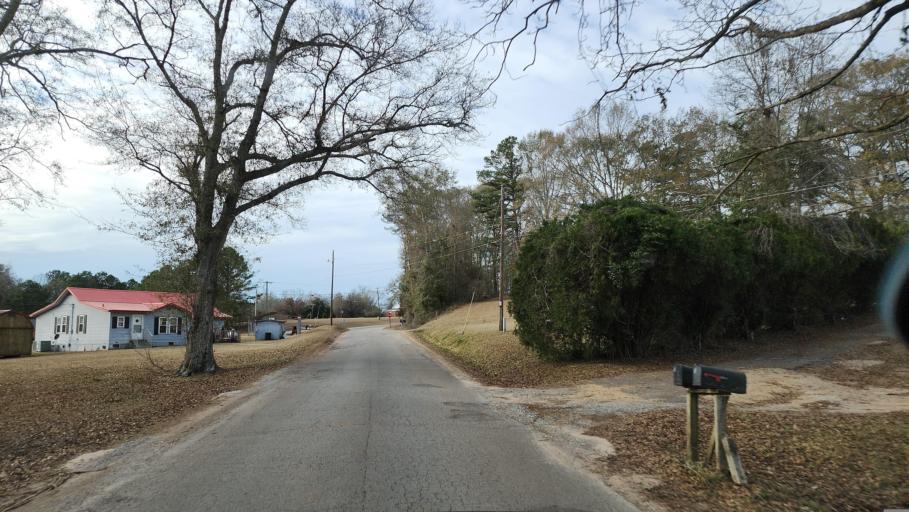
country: US
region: Mississippi
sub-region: Lauderdale County
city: Meridian
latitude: 32.2581
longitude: -88.7005
